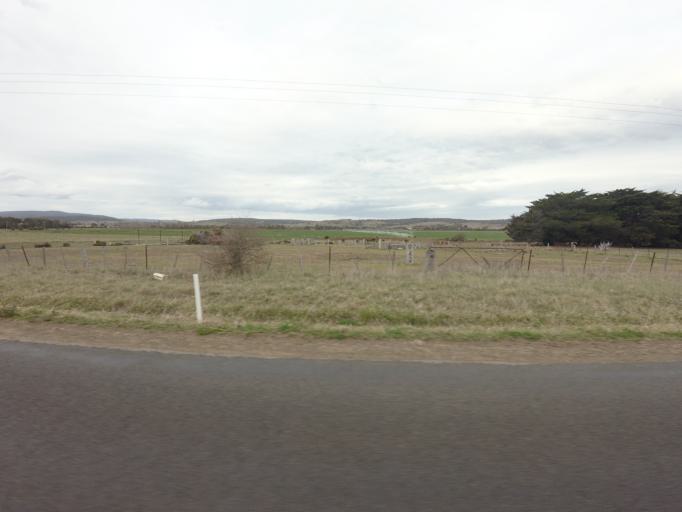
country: AU
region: Tasmania
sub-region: Break O'Day
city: St Helens
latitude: -42.0021
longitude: 148.0674
